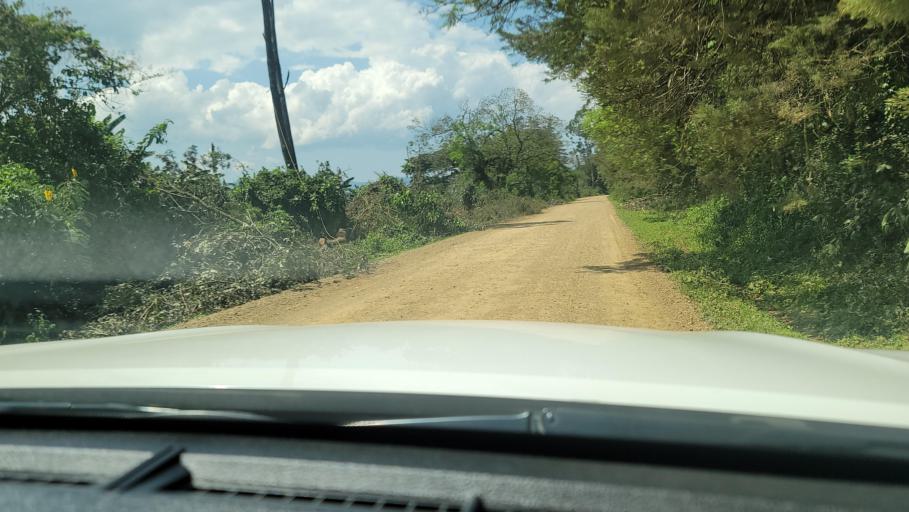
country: ET
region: Oromiya
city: Agaro
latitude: 7.7894
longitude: 36.4301
